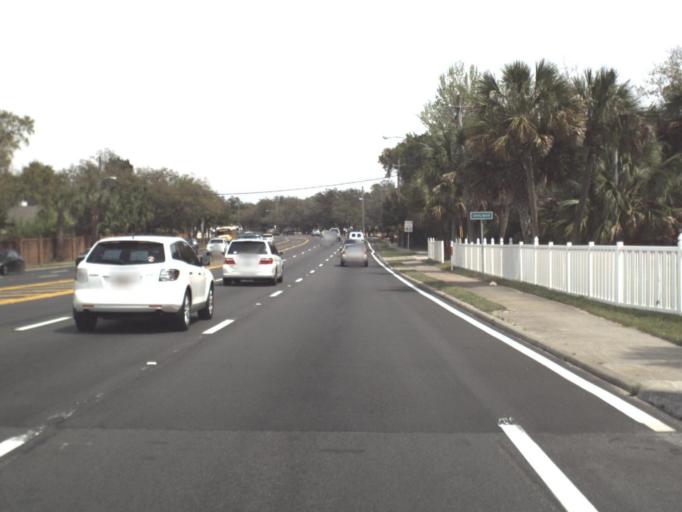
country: US
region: Florida
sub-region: Okaloosa County
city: Lake Lorraine
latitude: 30.4398
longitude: -86.5877
